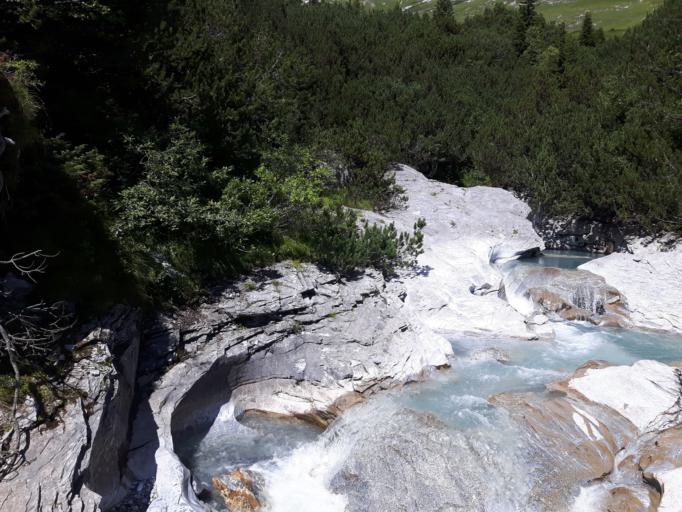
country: CH
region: Grisons
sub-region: Imboden District
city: Flims
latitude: 46.8629
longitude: 9.2528
